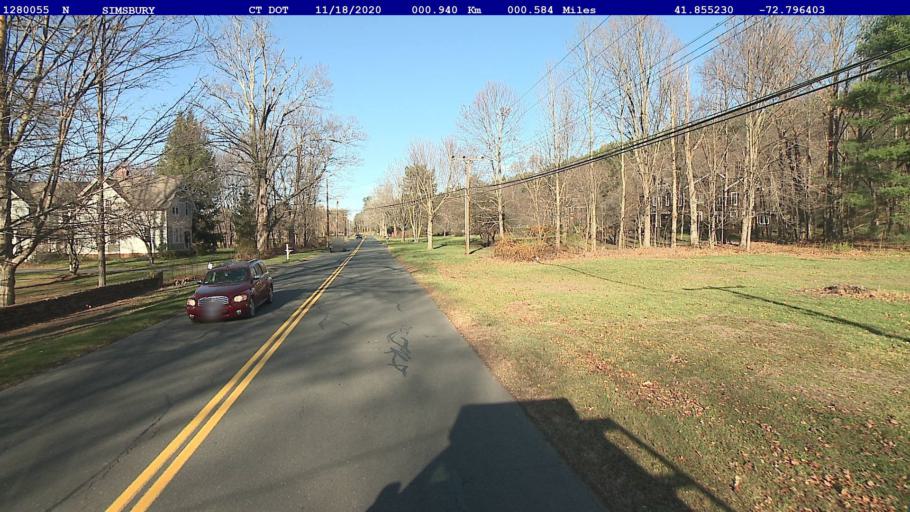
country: US
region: Connecticut
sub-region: Hartford County
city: Simsbury Center
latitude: 41.8552
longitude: -72.7964
